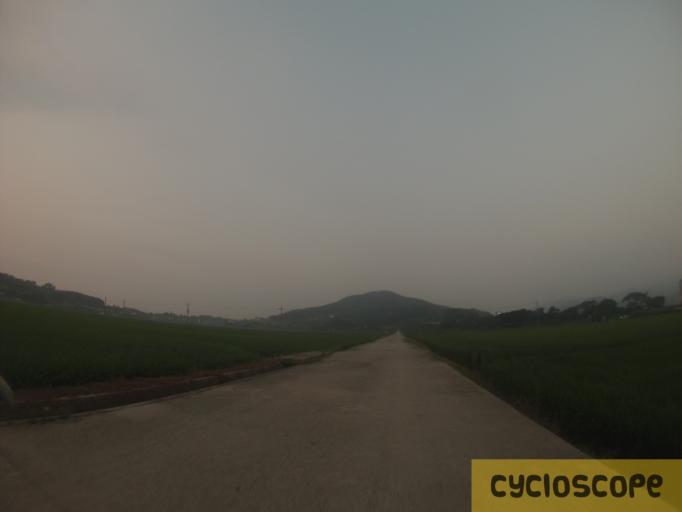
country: KR
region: Jeollabuk-do
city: Puan
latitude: 35.6538
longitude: 126.5001
